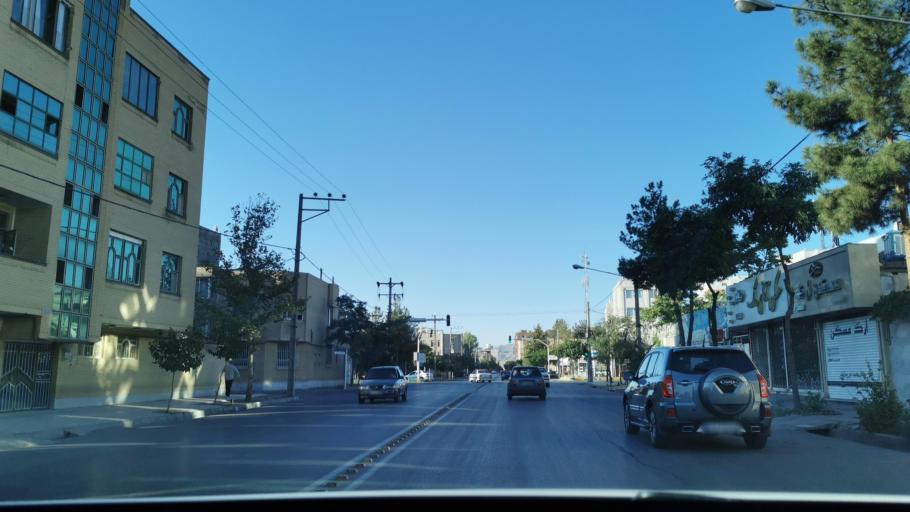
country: IR
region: Razavi Khorasan
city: Mashhad
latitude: 36.3530
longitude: 59.4974
